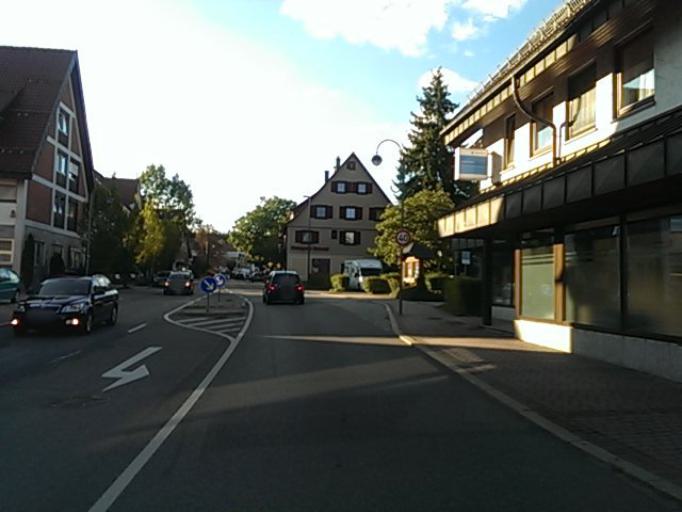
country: DE
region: Baden-Wuerttemberg
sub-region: Karlsruhe Region
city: Lossburg
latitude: 48.4123
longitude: 8.4524
